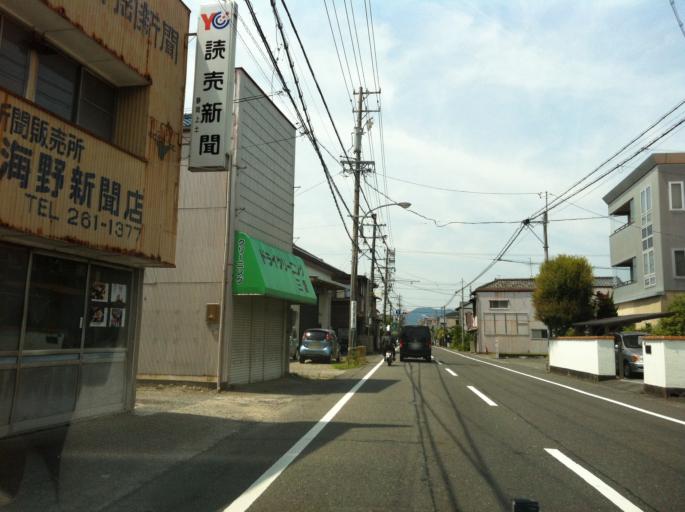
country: JP
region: Shizuoka
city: Shizuoka-shi
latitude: 34.9998
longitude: 138.4145
